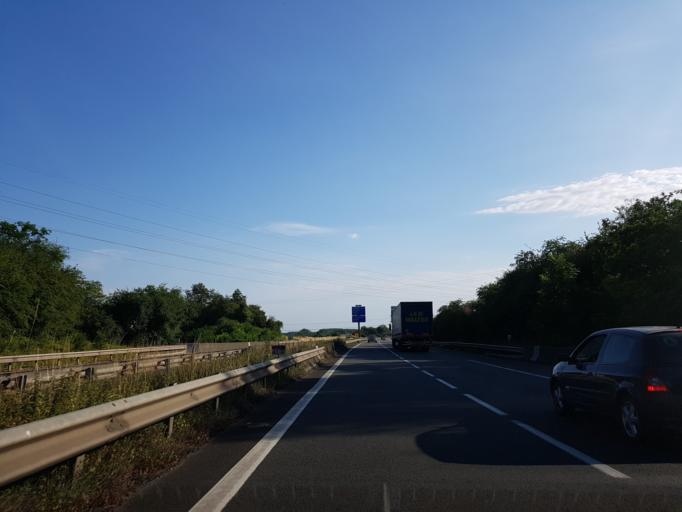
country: FR
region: Nord-Pas-de-Calais
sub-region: Departement du Nord
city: Hordain
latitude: 50.2588
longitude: 3.3268
